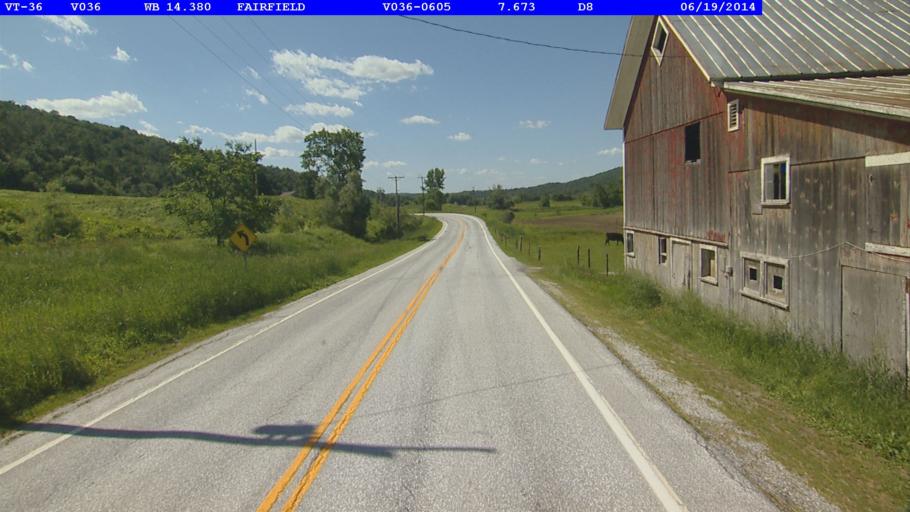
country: US
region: Vermont
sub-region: Franklin County
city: Enosburg Falls
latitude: 44.7981
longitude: -72.8879
